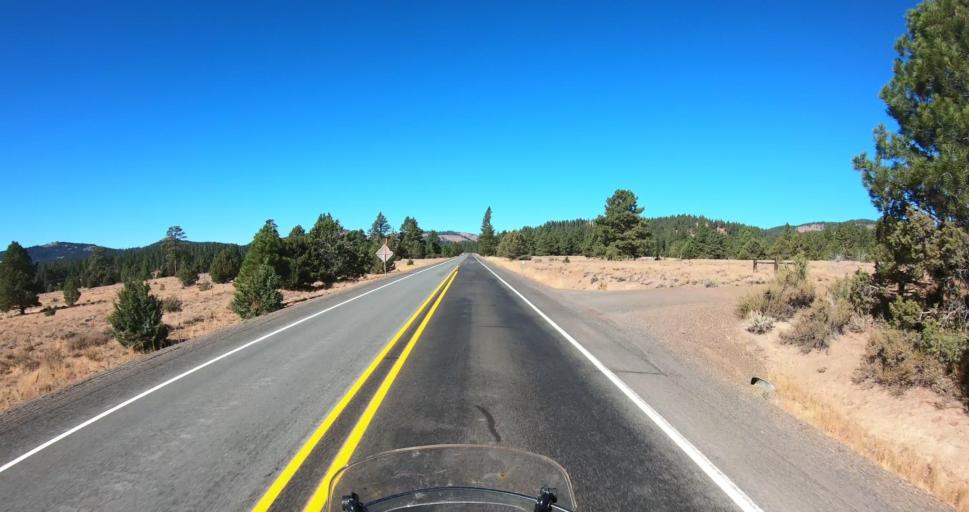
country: US
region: Oregon
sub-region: Lake County
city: Lakeview
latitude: 42.2264
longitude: -120.2346
